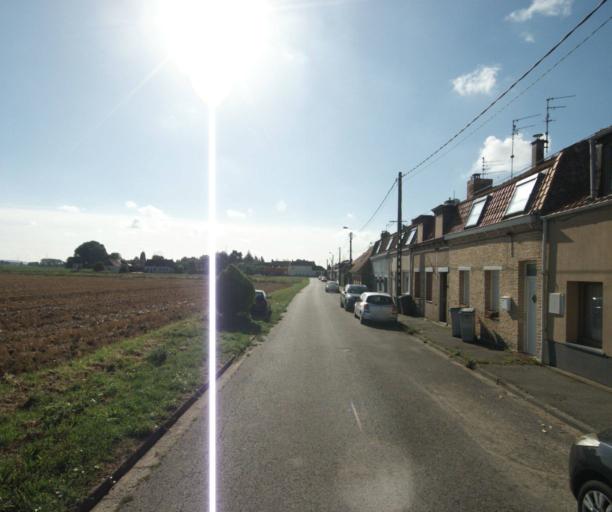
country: FR
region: Nord-Pas-de-Calais
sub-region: Departement du Nord
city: Toufflers
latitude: 50.6525
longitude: 3.2434
